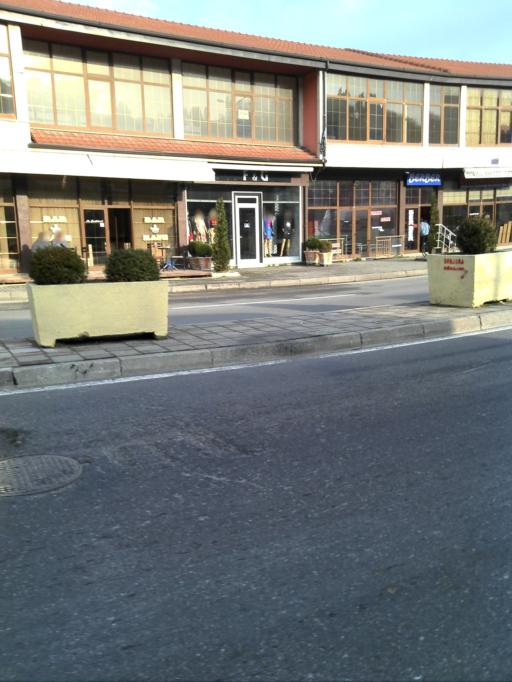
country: AL
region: Shkoder
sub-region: Rrethi i Shkodres
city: Shkoder
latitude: 42.0527
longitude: 19.4966
